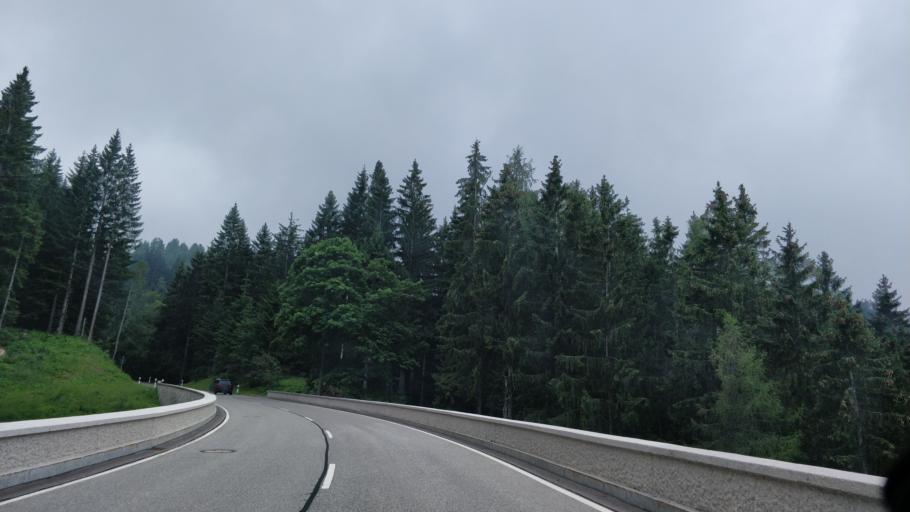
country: AT
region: Salzburg
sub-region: Politischer Bezirk Hallein
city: Hallein
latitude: 47.6382
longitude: 13.0916
